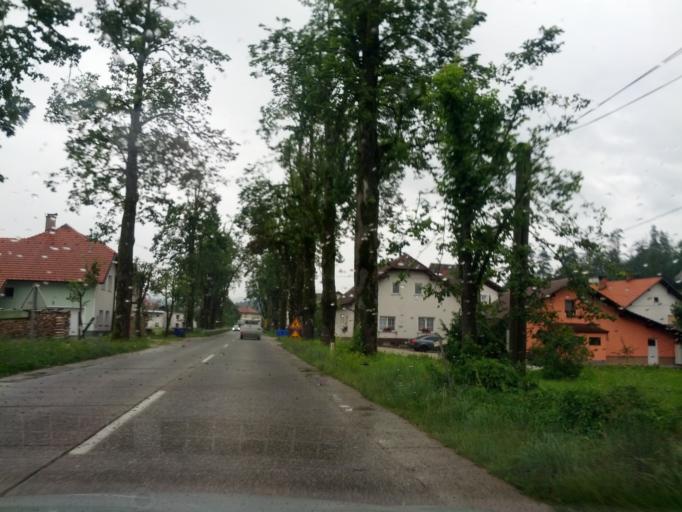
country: SI
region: Logatec
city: Logatec
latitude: 45.9223
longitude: 14.2295
